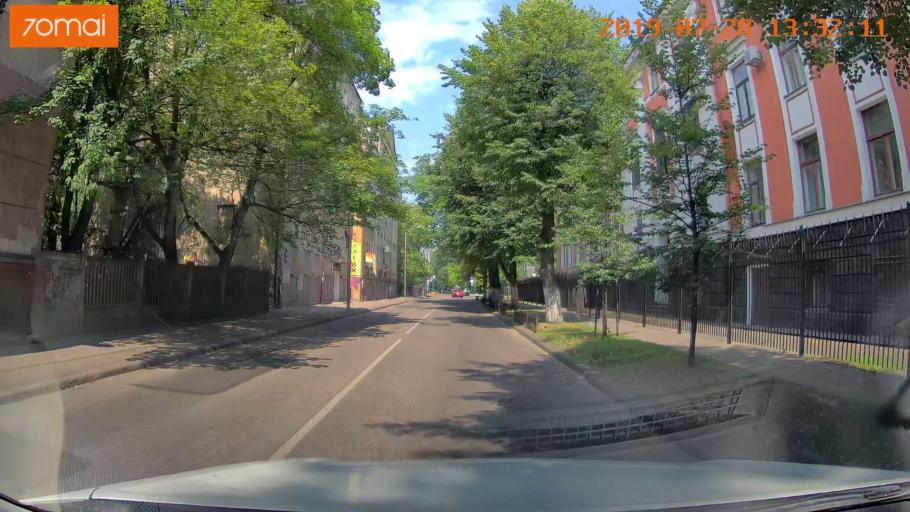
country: RU
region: Kaliningrad
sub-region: Gorod Kaliningrad
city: Kaliningrad
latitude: 54.7206
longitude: 20.4942
